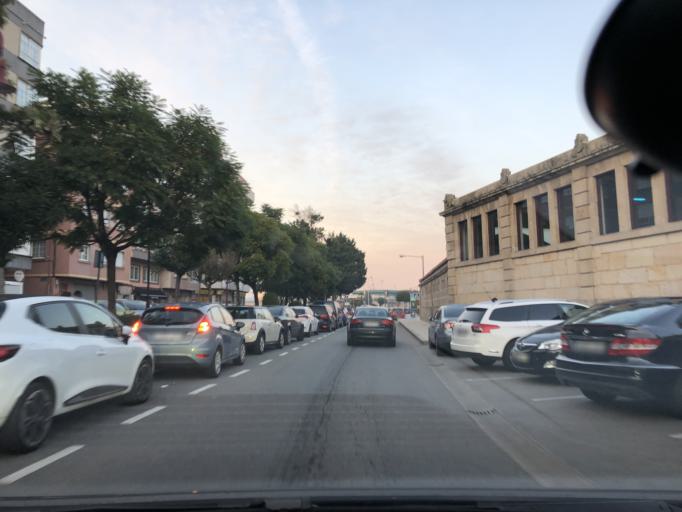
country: ES
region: Galicia
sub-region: Provincia de Pontevedra
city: Marin
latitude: 42.3923
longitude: -8.7052
